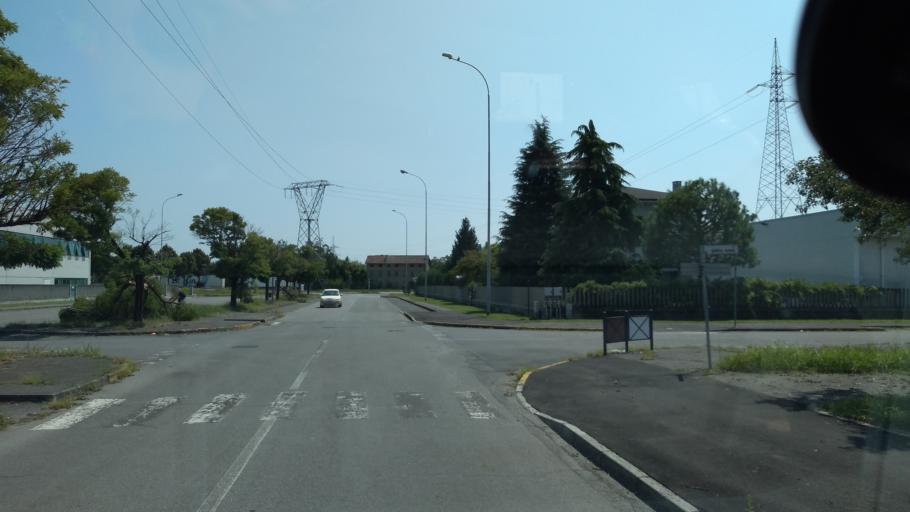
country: IT
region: Lombardy
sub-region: Provincia di Bergamo
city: Treviglio
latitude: 45.5129
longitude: 9.5800
